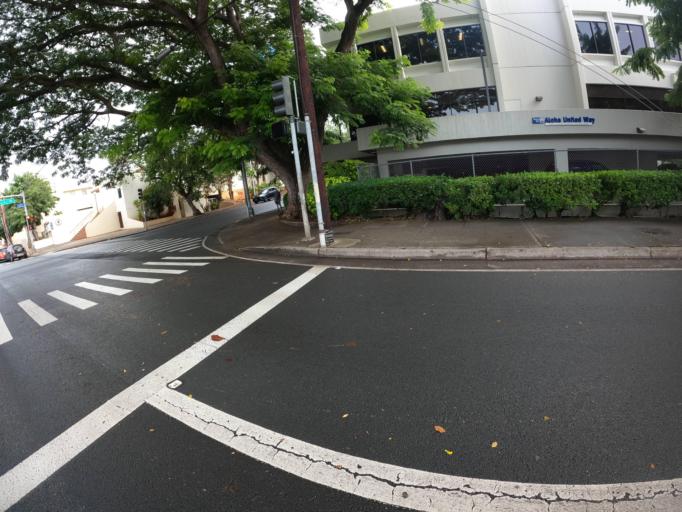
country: US
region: Hawaii
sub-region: Honolulu County
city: Honolulu
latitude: 21.3173
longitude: -157.8599
